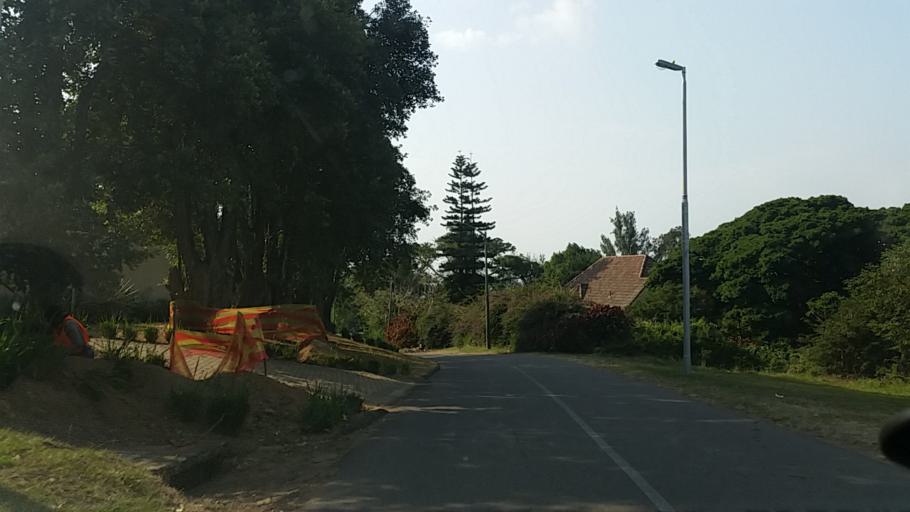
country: ZA
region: KwaZulu-Natal
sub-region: eThekwini Metropolitan Municipality
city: Berea
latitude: -29.8322
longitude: 30.9397
